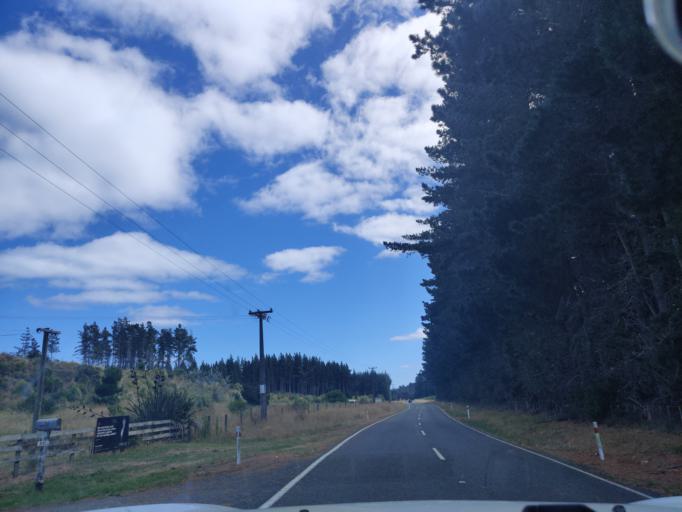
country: NZ
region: Manawatu-Wanganui
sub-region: Horowhenua District
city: Foxton
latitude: -40.3782
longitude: 175.2554
